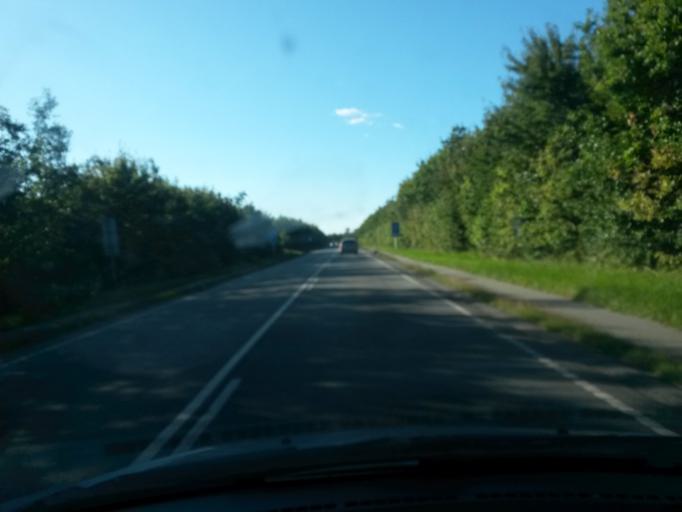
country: DK
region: Central Jutland
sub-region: Arhus Kommune
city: Sabro
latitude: 56.2169
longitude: 9.9905
